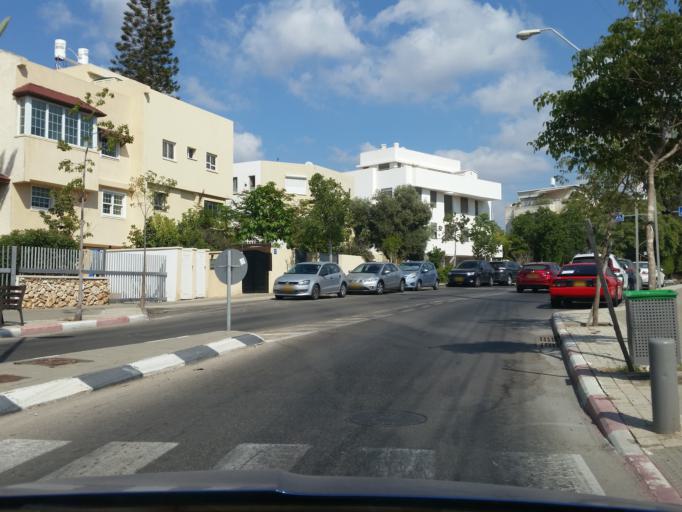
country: IL
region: Tel Aviv
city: Ramat HaSharon
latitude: 32.1163
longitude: 34.8301
